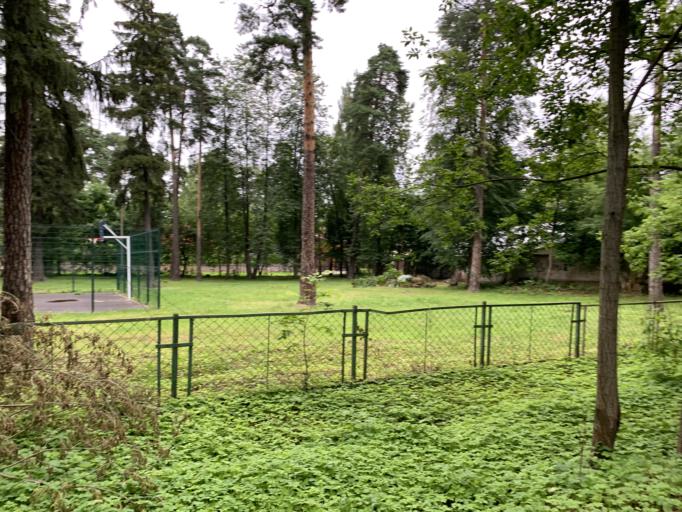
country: RU
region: Moskovskaya
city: Mamontovka
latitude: 55.9752
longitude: 37.8252
